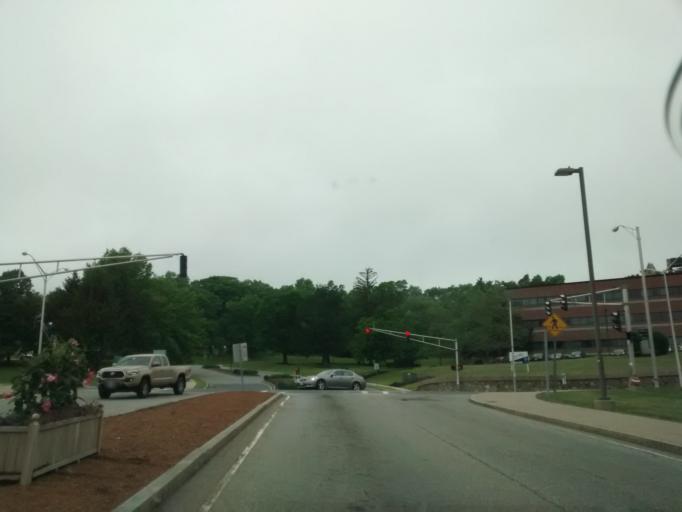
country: US
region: Massachusetts
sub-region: Worcester County
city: Hamilton
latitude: 42.2762
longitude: -71.7652
